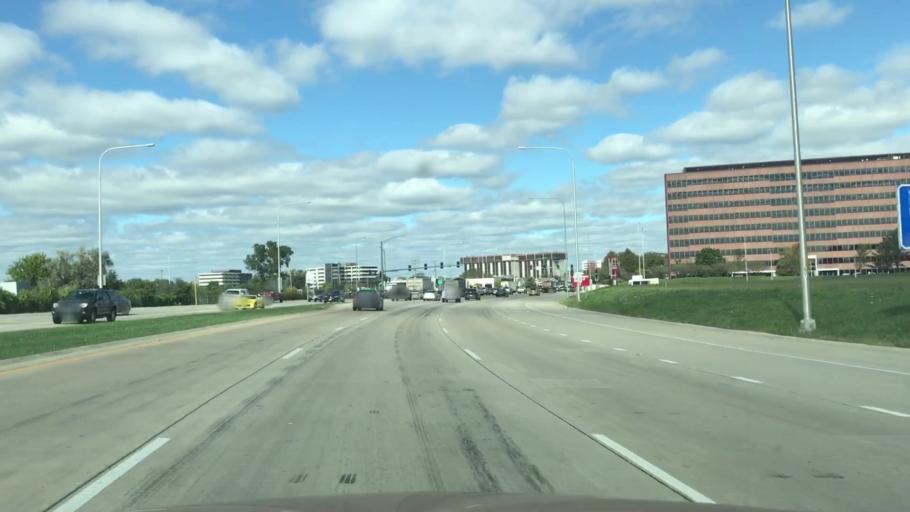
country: US
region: Illinois
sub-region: Cook County
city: Rosemont
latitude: 41.9931
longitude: -87.8840
